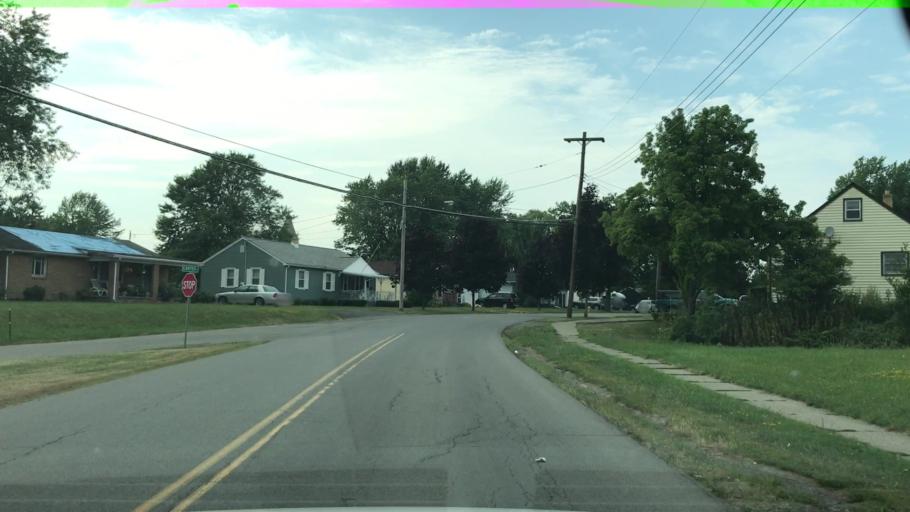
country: US
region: New York
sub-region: Erie County
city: Lancaster
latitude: 42.9062
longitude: -78.6735
